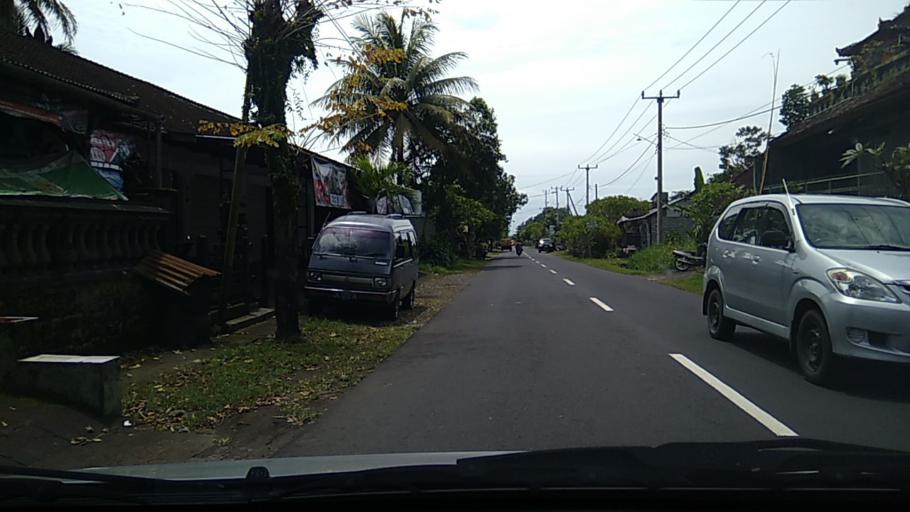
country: ID
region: Bali
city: Wanasari Baleran
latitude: -8.4735
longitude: 115.1367
